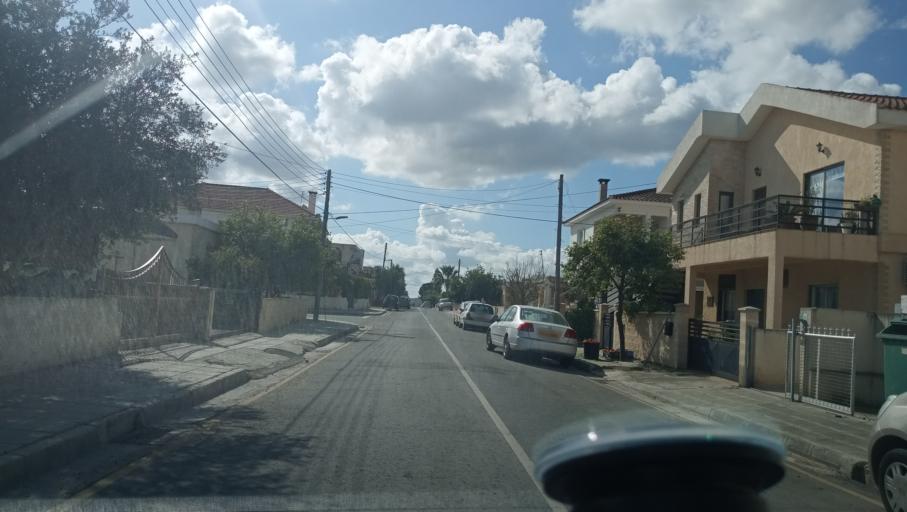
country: CY
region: Lefkosia
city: Geri
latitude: 35.1015
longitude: 33.4054
